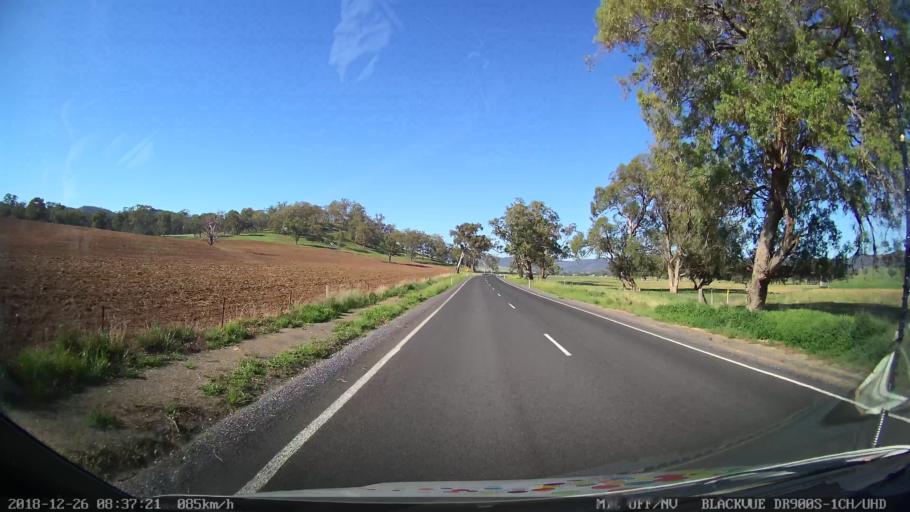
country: AU
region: New South Wales
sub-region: Upper Hunter Shire
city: Merriwa
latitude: -32.4314
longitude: 150.0910
